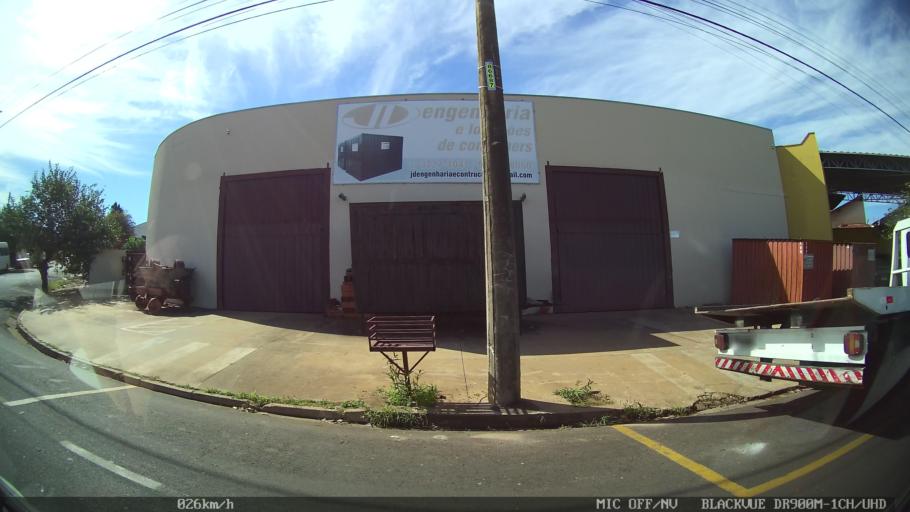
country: BR
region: Sao Paulo
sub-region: Sao Jose Do Rio Preto
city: Sao Jose do Rio Preto
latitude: -20.8475
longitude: -49.3688
